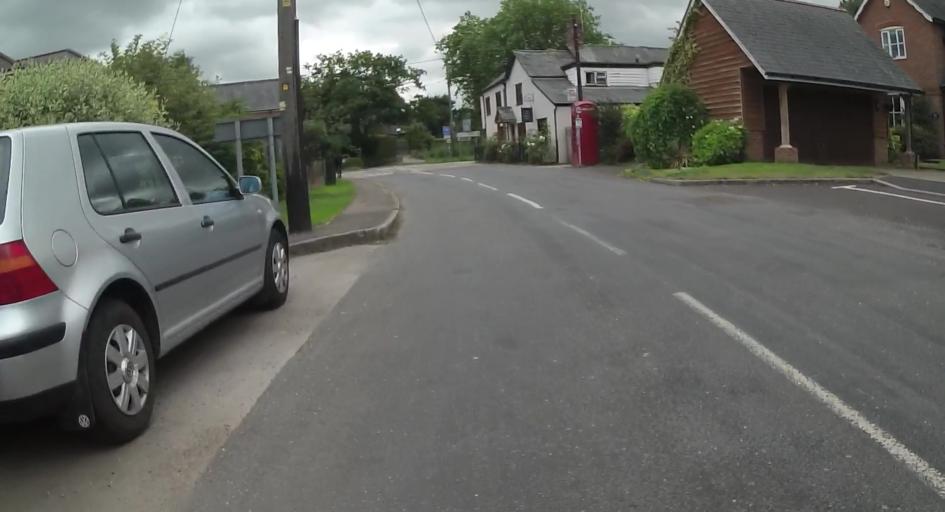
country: GB
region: England
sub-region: Hampshire
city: Swanmore
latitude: 51.0472
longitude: -1.1610
